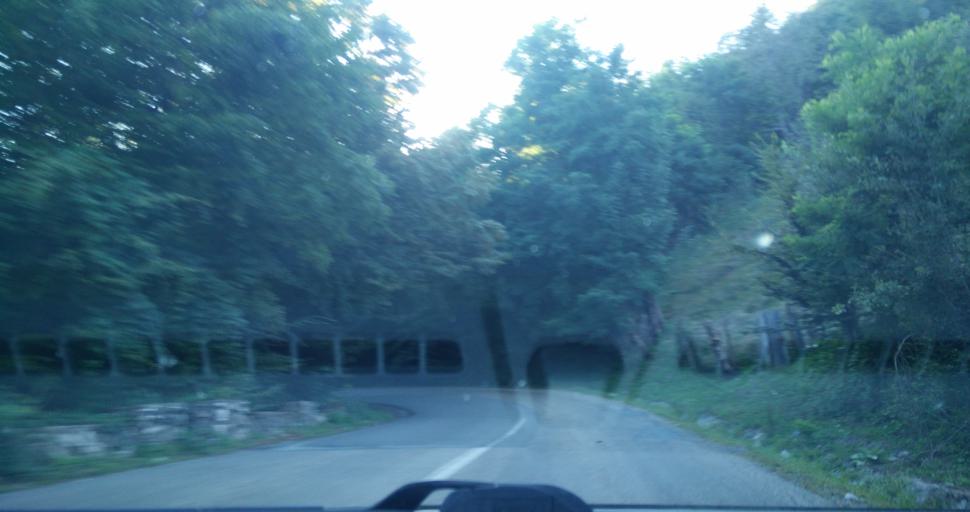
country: RO
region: Bihor
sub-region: Oras Nucet
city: Nucet
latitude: 46.4876
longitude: 22.6082
